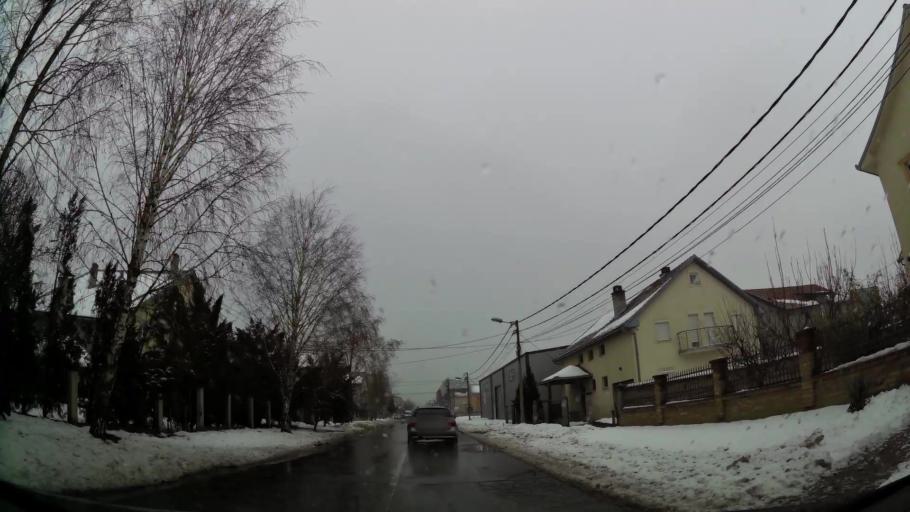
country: RS
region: Central Serbia
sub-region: Belgrade
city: Zemun
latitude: 44.8545
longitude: 20.3451
